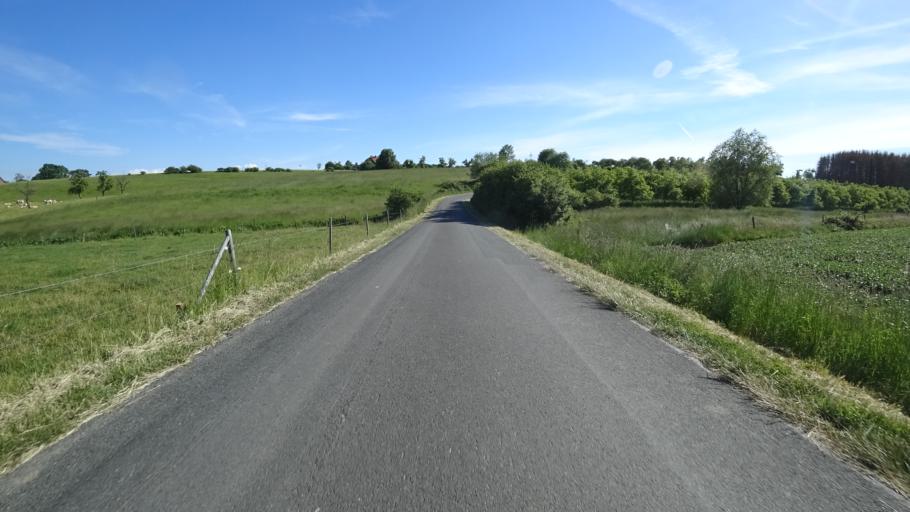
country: DE
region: North Rhine-Westphalia
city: Oelde
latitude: 51.7828
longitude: 8.1943
